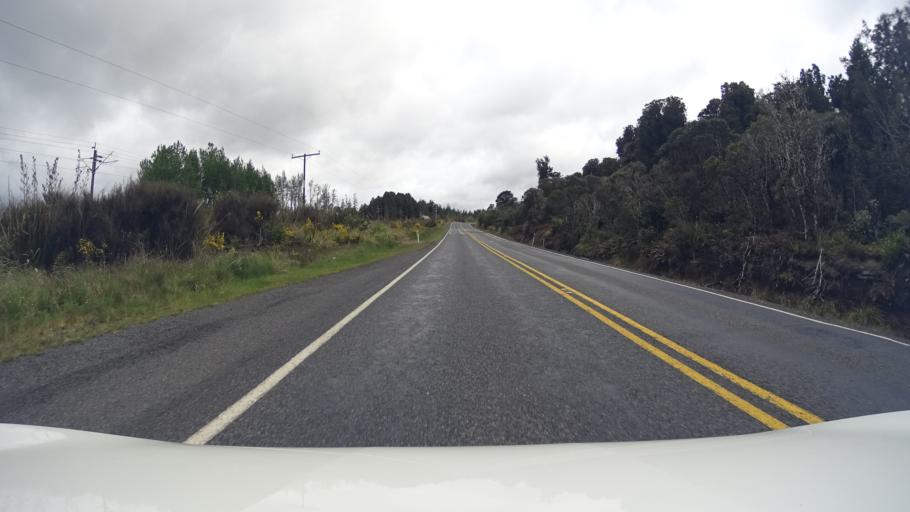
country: NZ
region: Manawatu-Wanganui
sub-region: Ruapehu District
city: Waiouru
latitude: -39.2571
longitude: 175.3882
